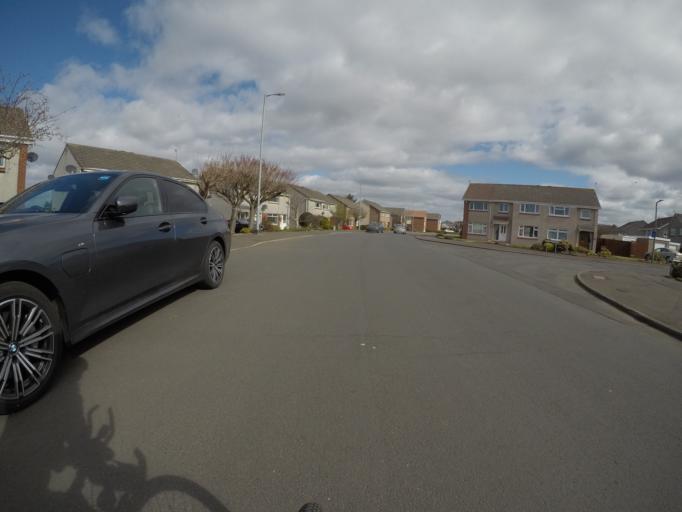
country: GB
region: Scotland
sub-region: South Ayrshire
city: Troon
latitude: 55.5642
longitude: -4.6454
